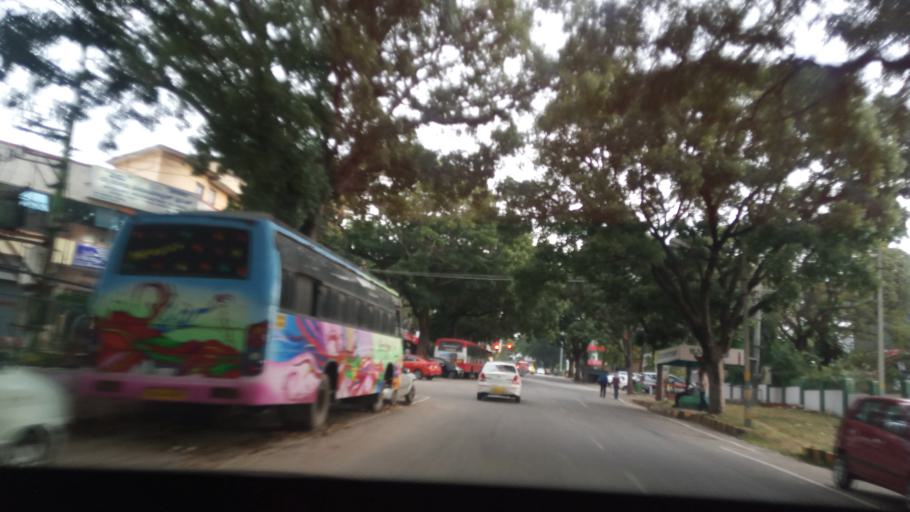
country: IN
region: Karnataka
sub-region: Mysore
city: Mysore
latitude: 12.3271
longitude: 76.6322
